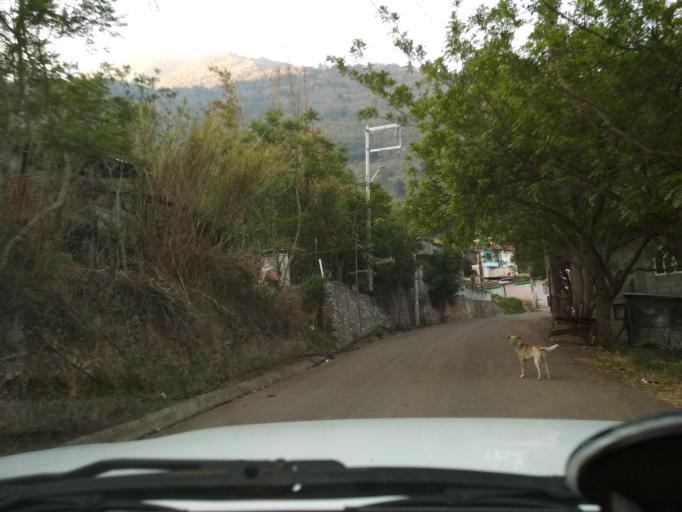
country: MX
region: Veracruz
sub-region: Nogales
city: Taza de Agua Ojo Zarco
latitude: 18.7728
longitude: -97.1945
